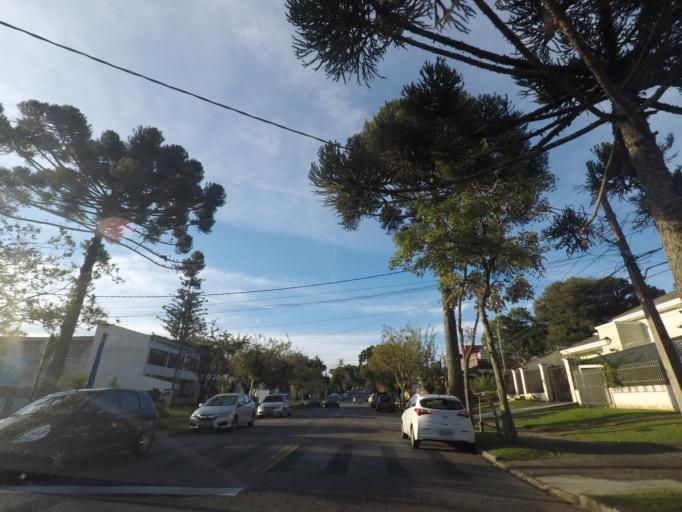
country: BR
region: Parana
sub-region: Curitiba
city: Curitiba
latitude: -25.4042
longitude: -49.2653
